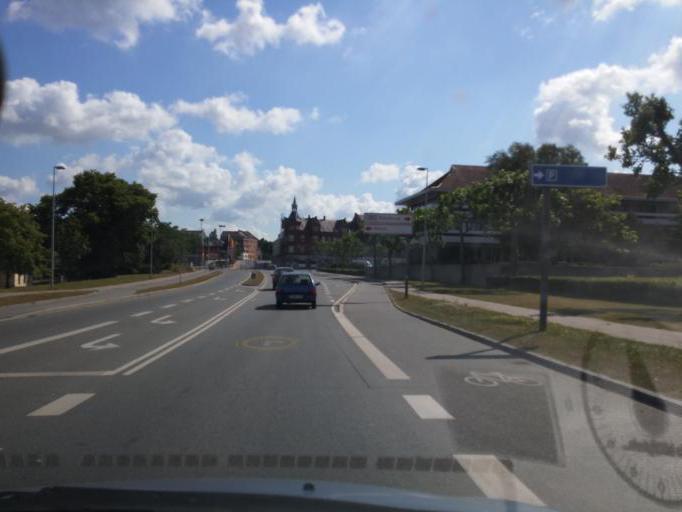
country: DK
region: South Denmark
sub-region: Odense Kommune
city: Odense
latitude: 55.4057
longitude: 10.3824
